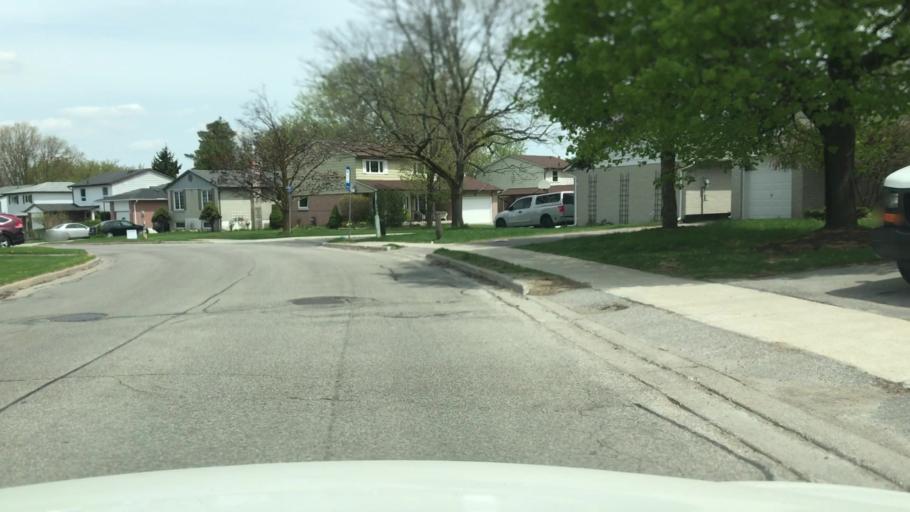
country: CA
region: Ontario
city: Newmarket
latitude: 44.0397
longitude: -79.4691
